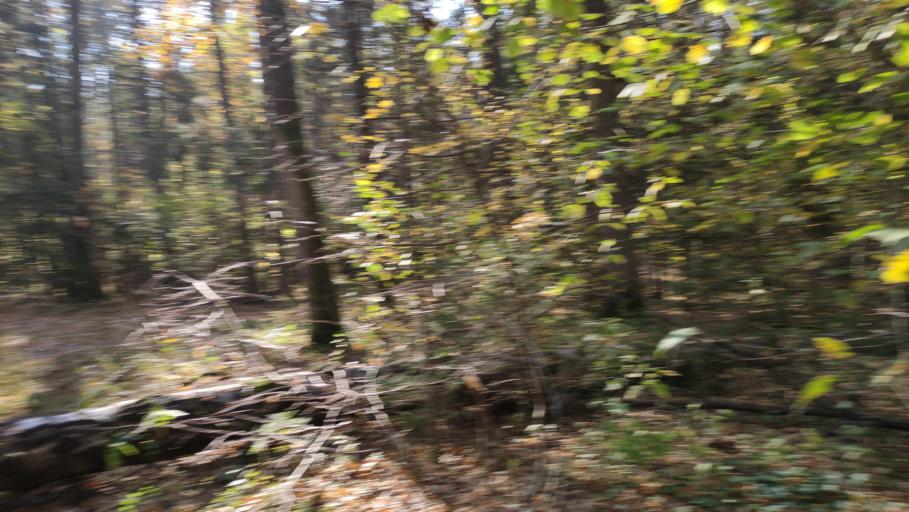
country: LT
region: Alytaus apskritis
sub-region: Alytus
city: Alytus
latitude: 54.3853
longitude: 24.0860
